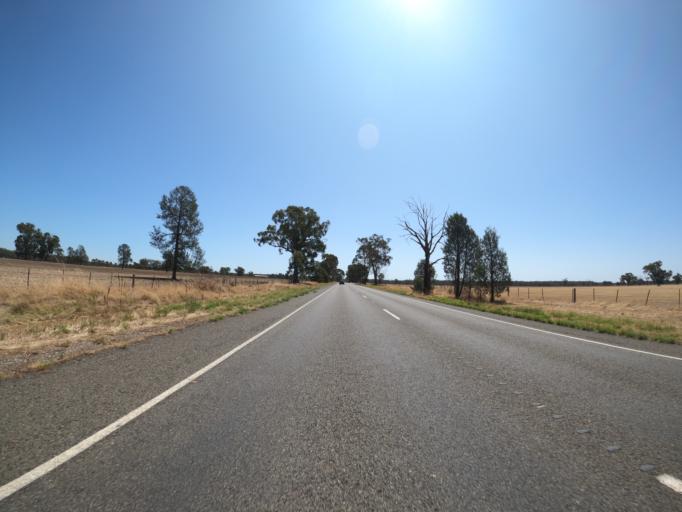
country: AU
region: New South Wales
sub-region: Corowa Shire
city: Corowa
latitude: -36.0717
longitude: 146.2210
